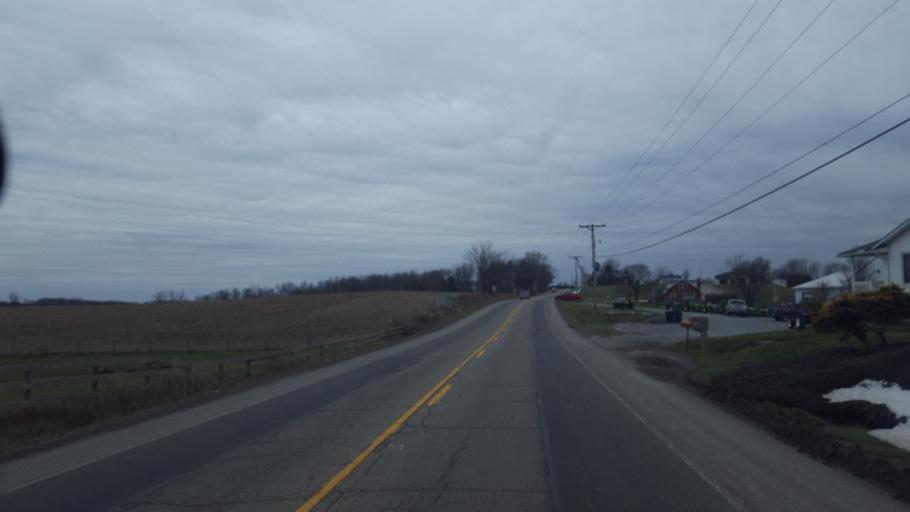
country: US
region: Ohio
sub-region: Tuscarawas County
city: Sugarcreek
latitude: 40.6098
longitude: -81.7084
